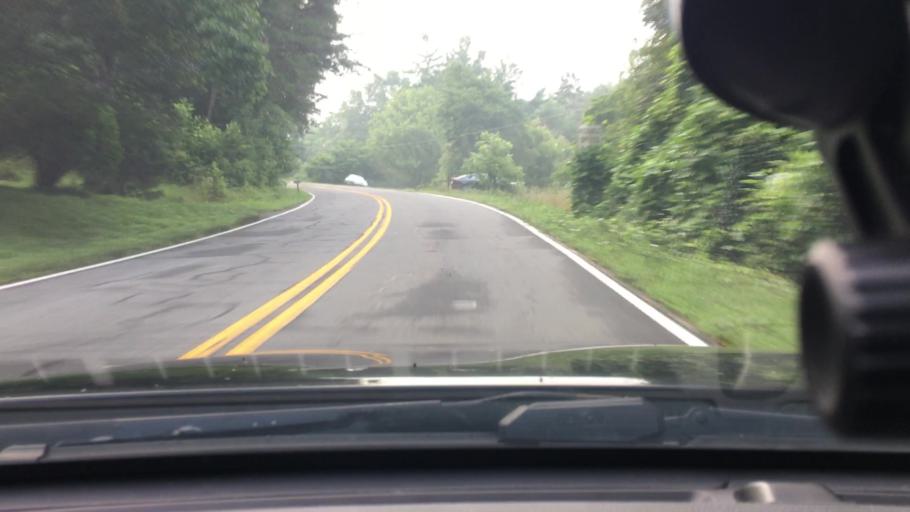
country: US
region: North Carolina
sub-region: Rutherford County
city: Rutherfordton
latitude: 35.3776
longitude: -81.9794
